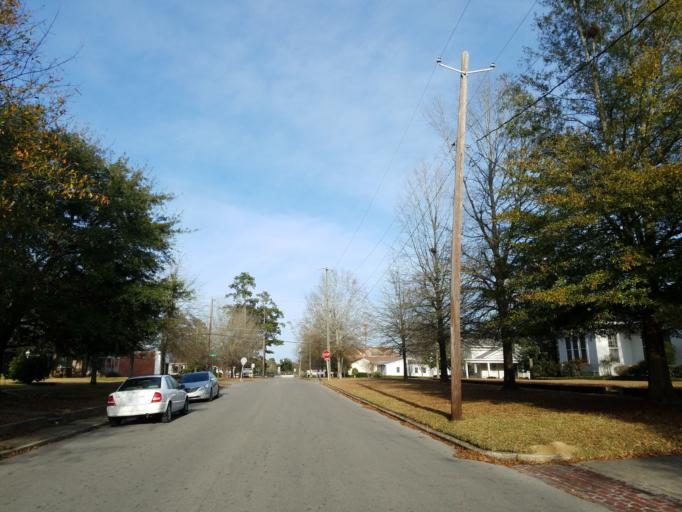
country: US
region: Mississippi
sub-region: Forrest County
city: Hattiesburg
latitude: 31.3233
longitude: -89.2990
